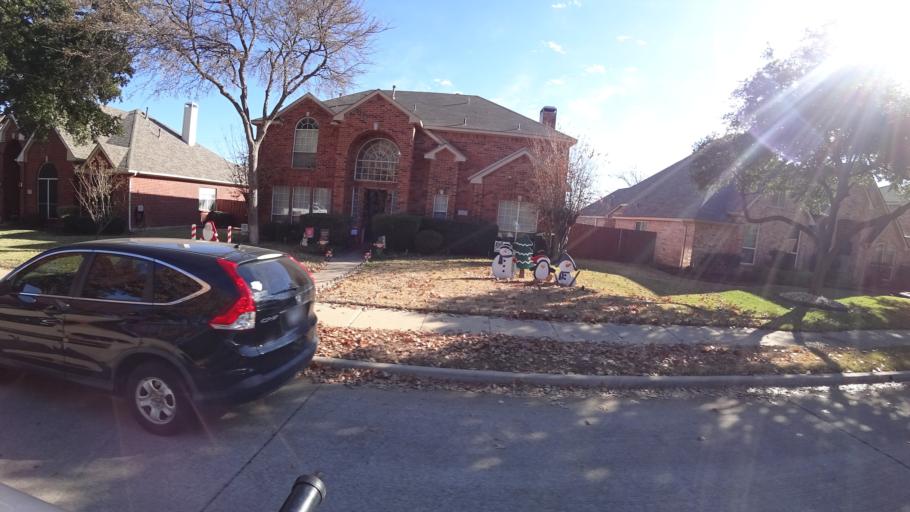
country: US
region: Texas
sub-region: Denton County
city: Lewisville
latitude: 33.0121
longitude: -97.0326
